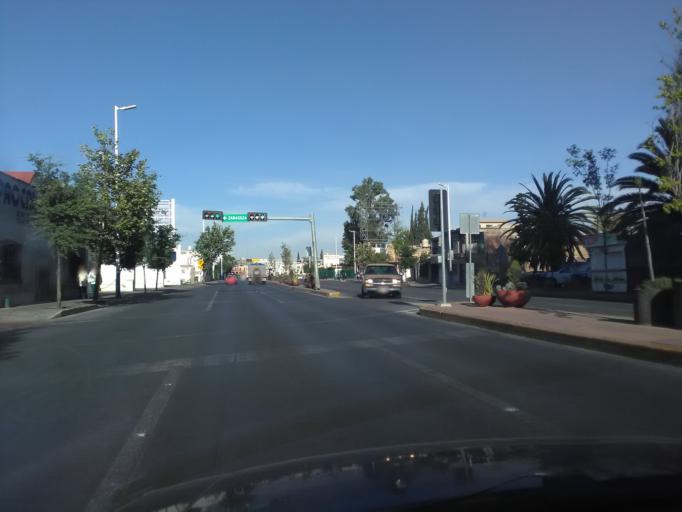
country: MX
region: Durango
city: Victoria de Durango
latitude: 24.0346
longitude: -104.6733
